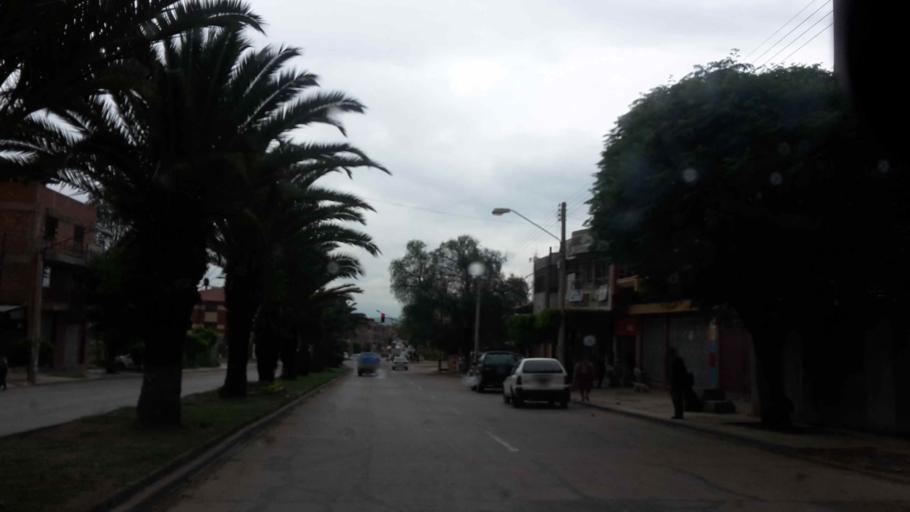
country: BO
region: Cochabamba
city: Cochabamba
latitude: -17.4291
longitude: -66.1543
